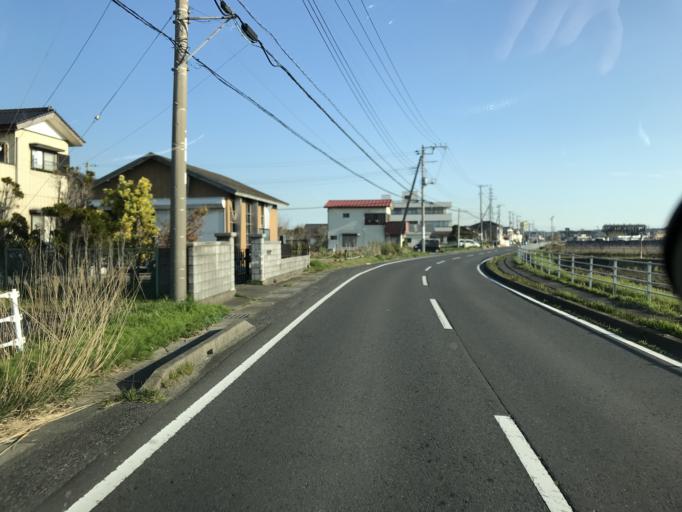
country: JP
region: Chiba
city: Asahi
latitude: 35.7178
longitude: 140.6833
